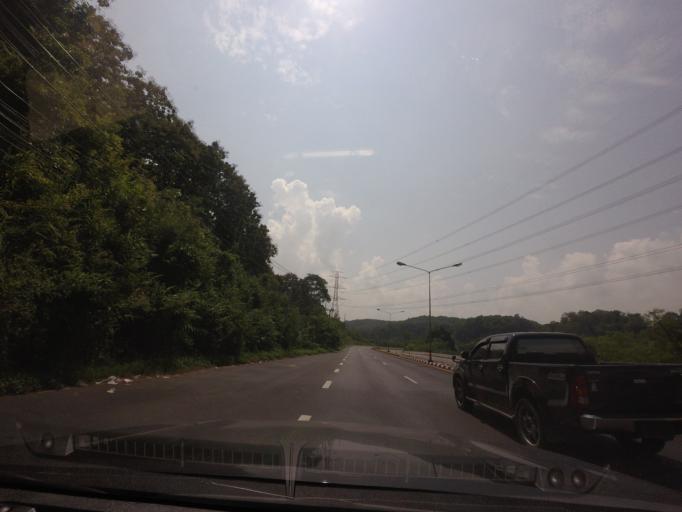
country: TH
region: Phrae
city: Den Chai
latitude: 17.8891
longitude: 100.0490
